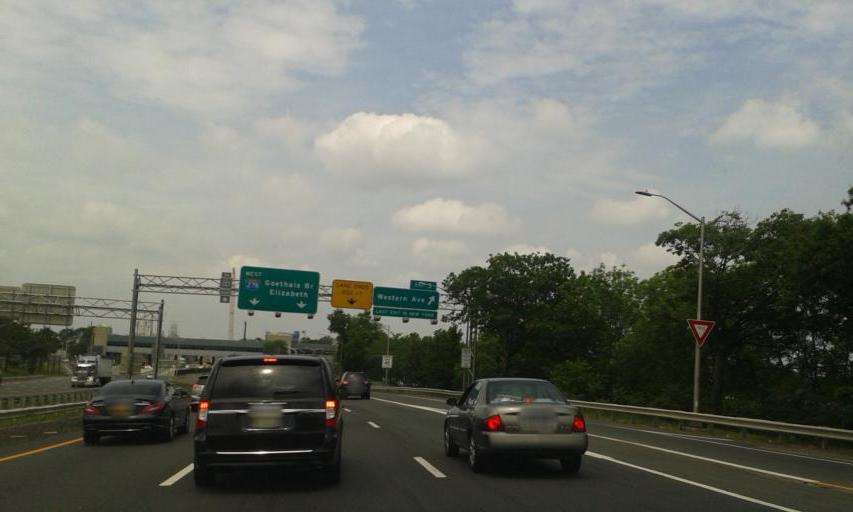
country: US
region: New York
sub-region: Richmond County
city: Bloomfield
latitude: 40.6260
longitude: -74.1787
